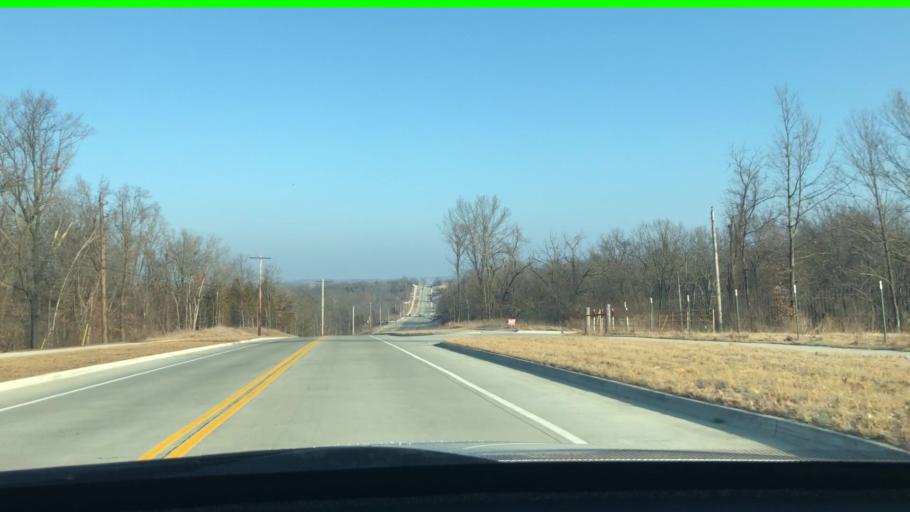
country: US
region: Missouri
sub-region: Boone County
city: Columbia
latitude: 38.8977
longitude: -92.4005
